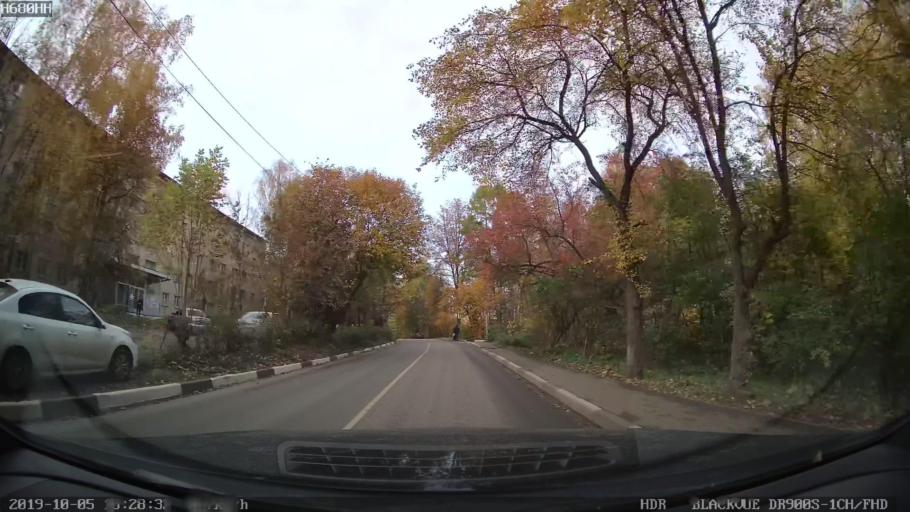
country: RU
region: Moskovskaya
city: Solnechnogorsk
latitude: 56.2166
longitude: 37.0283
